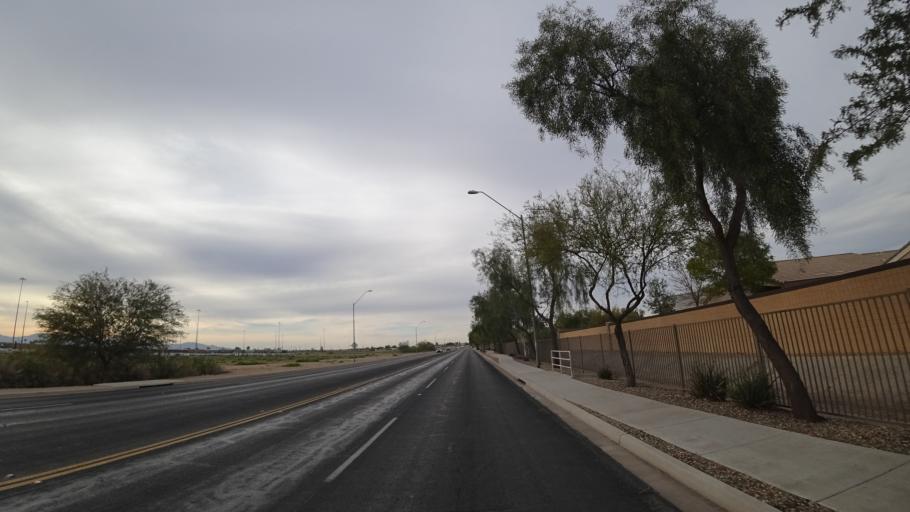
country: US
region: Arizona
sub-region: Maricopa County
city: El Mirage
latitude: 33.6188
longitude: -112.3169
